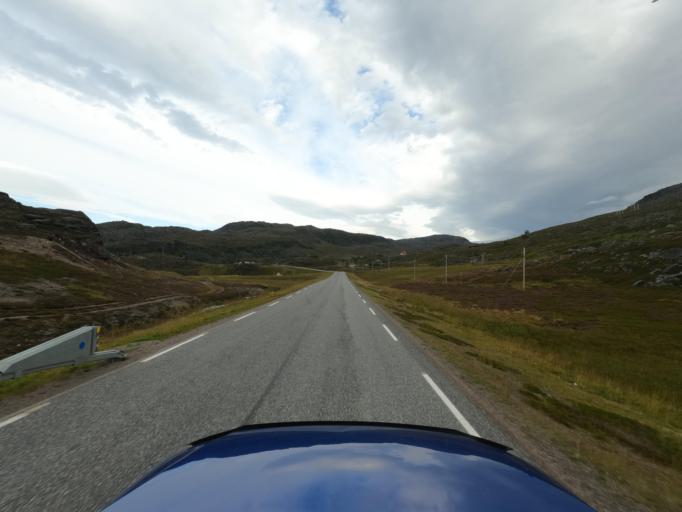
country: NO
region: Finnmark Fylke
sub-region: Hammerfest
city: Rypefjord
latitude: 70.5979
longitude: 23.6839
